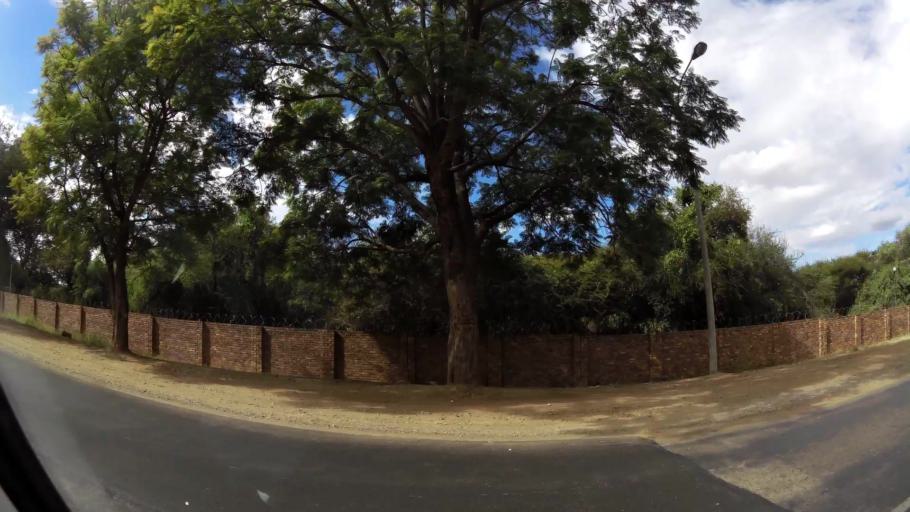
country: ZA
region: Limpopo
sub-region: Waterberg District Municipality
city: Warmbaths
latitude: -24.8879
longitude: 28.2845
